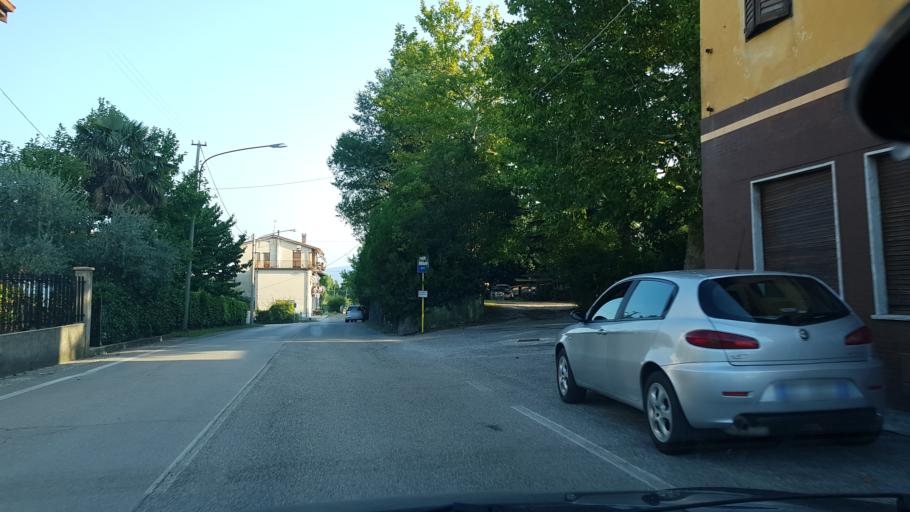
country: IT
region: Friuli Venezia Giulia
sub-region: Provincia di Gorizia
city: San Floriano del Collio
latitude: 45.9710
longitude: 13.6134
